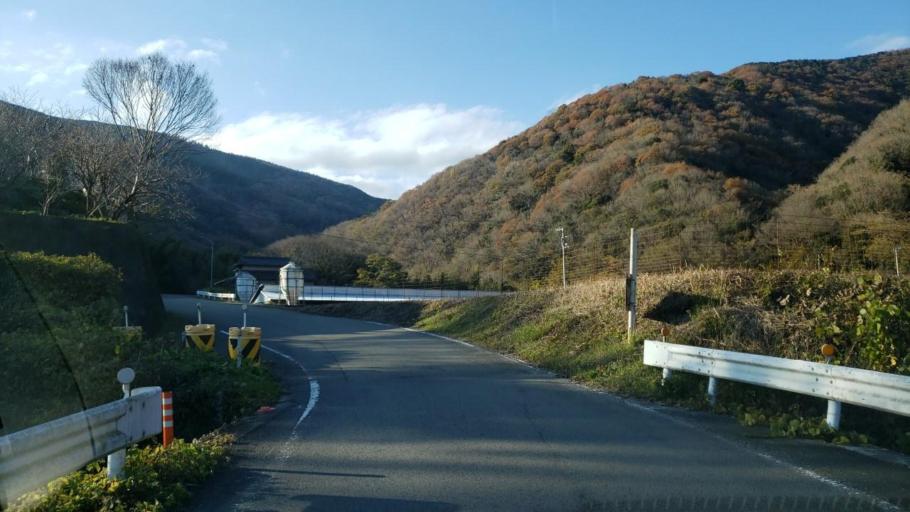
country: JP
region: Tokushima
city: Wakimachi
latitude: 34.0752
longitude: 134.0832
